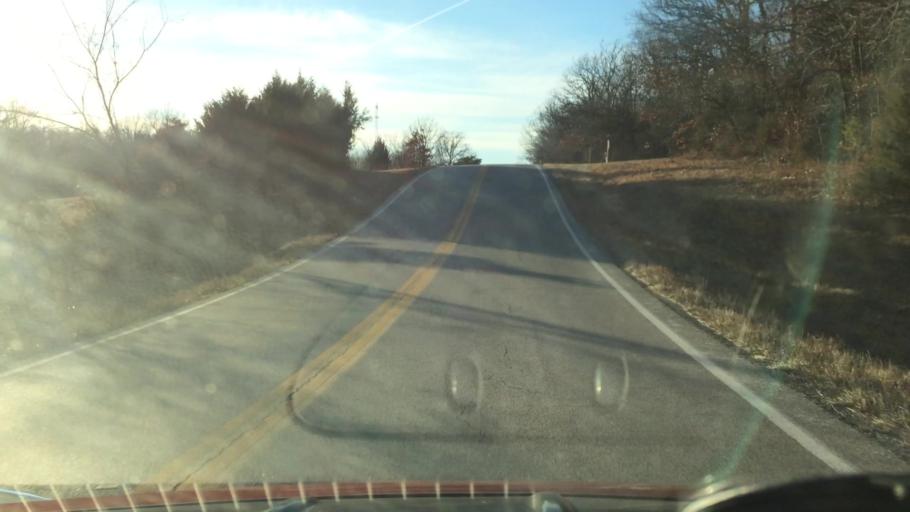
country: US
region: Missouri
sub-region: Webster County
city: Marshfield
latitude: 37.3409
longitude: -92.9751
